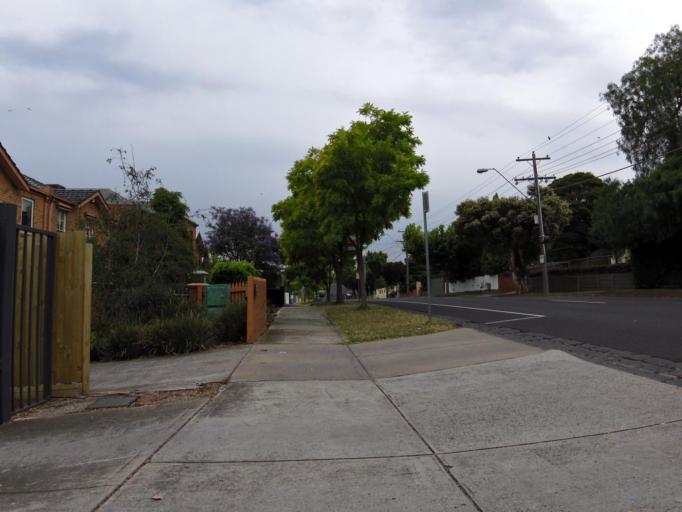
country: AU
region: Victoria
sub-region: Melbourne
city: Ascot Vale
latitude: -37.7866
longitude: 144.9050
